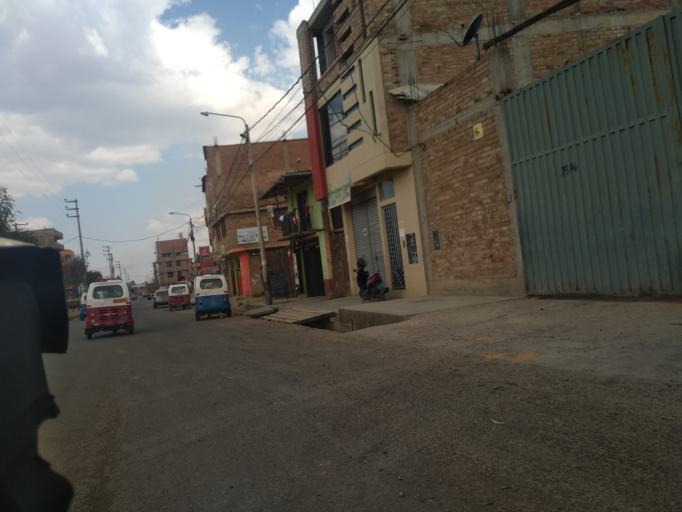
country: PE
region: Cajamarca
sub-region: Provincia de Cajamarca
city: Cajamarca
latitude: -7.1749
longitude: -78.4914
